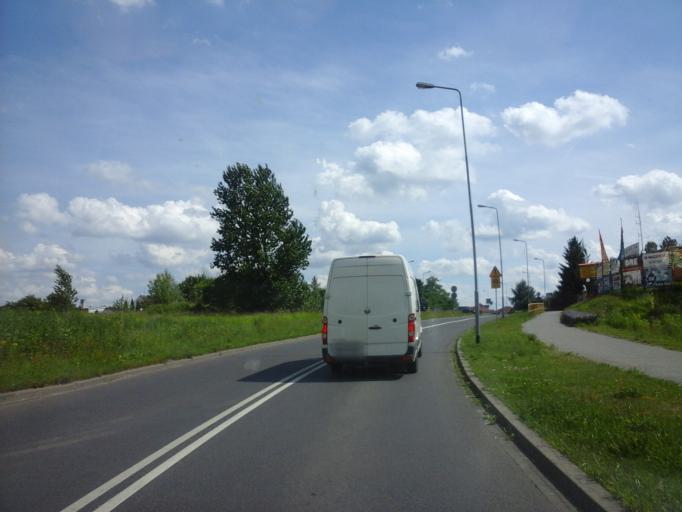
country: PL
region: West Pomeranian Voivodeship
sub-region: Powiat swidwinski
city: Swidwin
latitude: 53.7863
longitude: 15.7805
